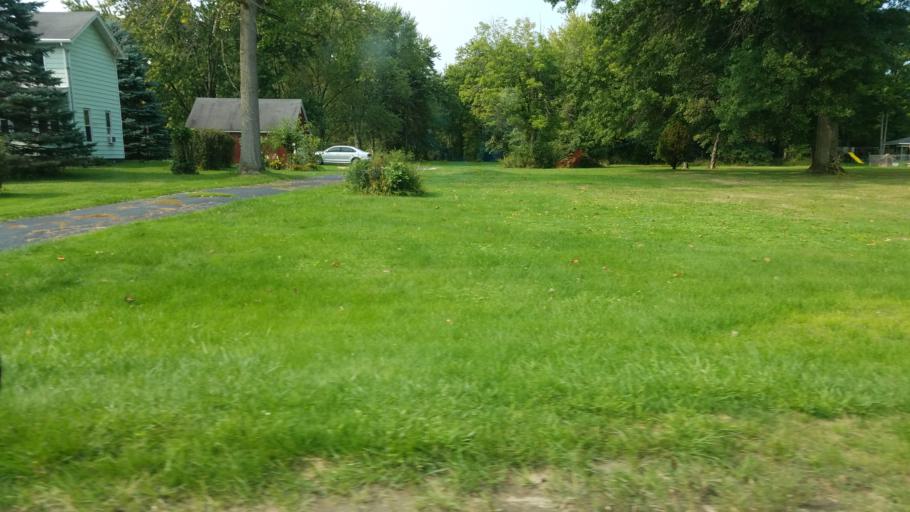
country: US
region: Ohio
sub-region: Mahoning County
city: Struthers
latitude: 41.0546
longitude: -80.6398
